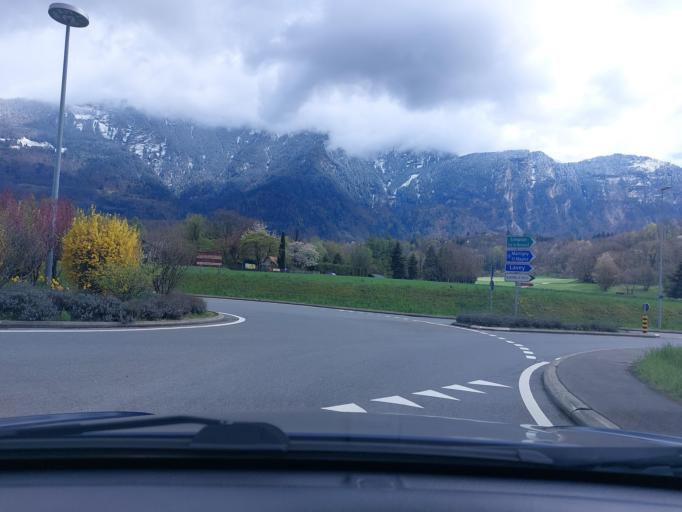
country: CH
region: Vaud
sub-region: Aigle District
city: Bex
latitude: 46.2437
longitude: 7.0021
